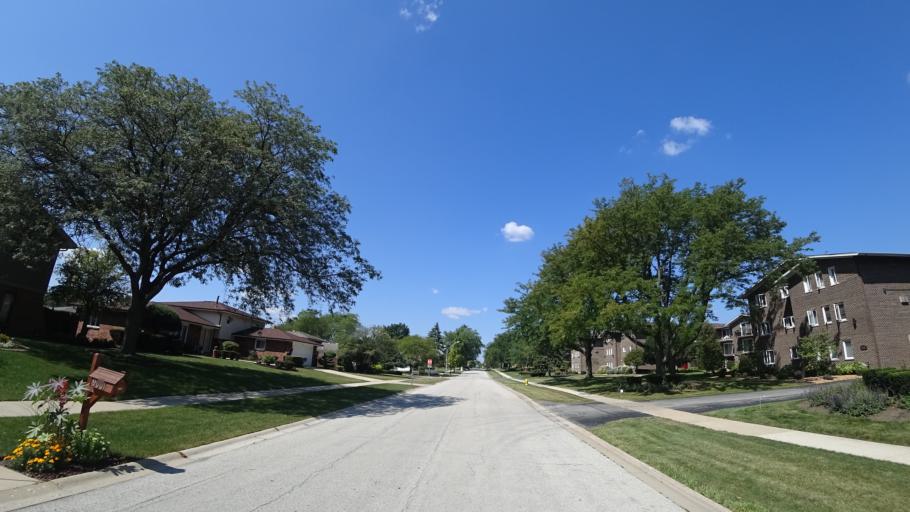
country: US
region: Illinois
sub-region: Cook County
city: Orland Park
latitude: 41.6364
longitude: -87.8392
